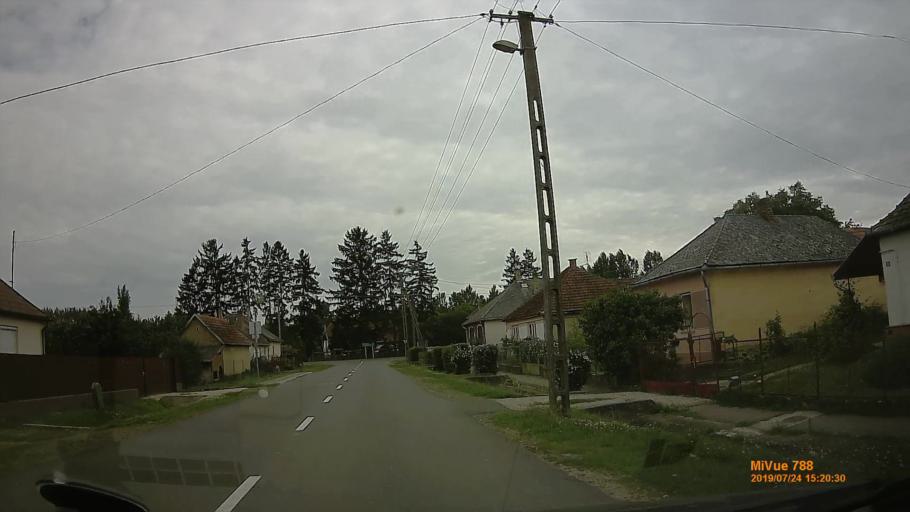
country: HU
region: Szabolcs-Szatmar-Bereg
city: Tarpa
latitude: 48.1622
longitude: 22.5446
